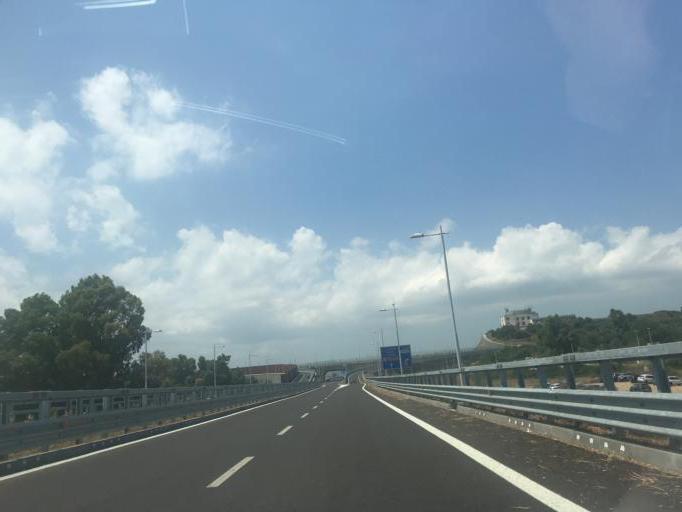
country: IT
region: Sardinia
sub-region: Provincia di Olbia-Tempio
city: Olbia
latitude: 40.9033
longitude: 9.5057
